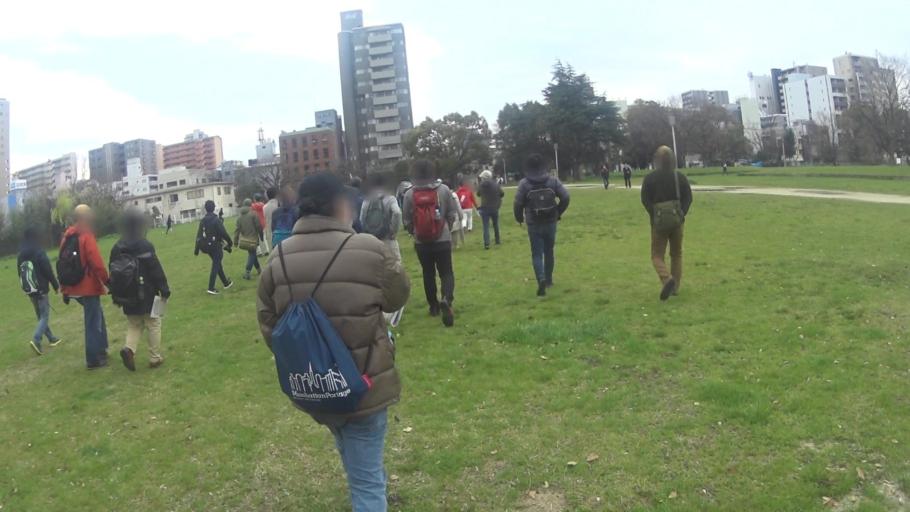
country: JP
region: Osaka
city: Osaka-shi
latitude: 34.6796
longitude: 135.5229
